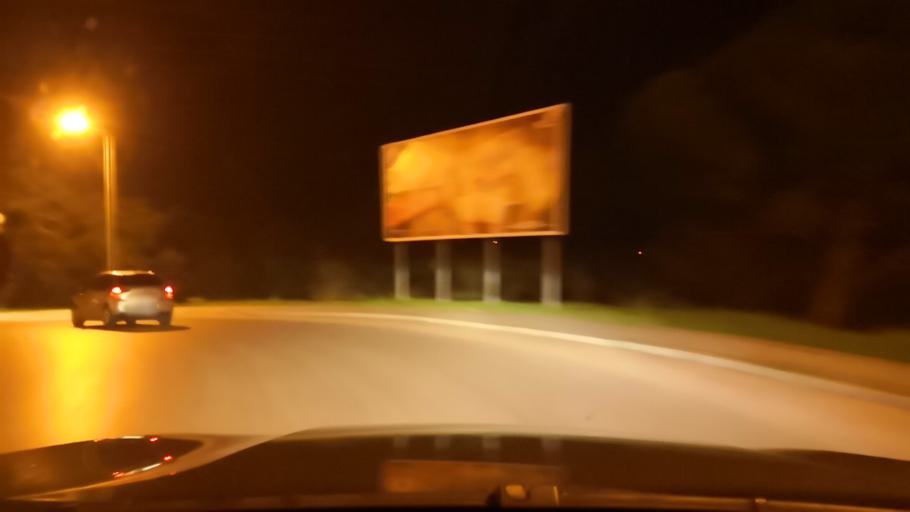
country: PT
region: Setubal
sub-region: Setubal
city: Setubal
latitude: 38.5418
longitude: -8.8633
